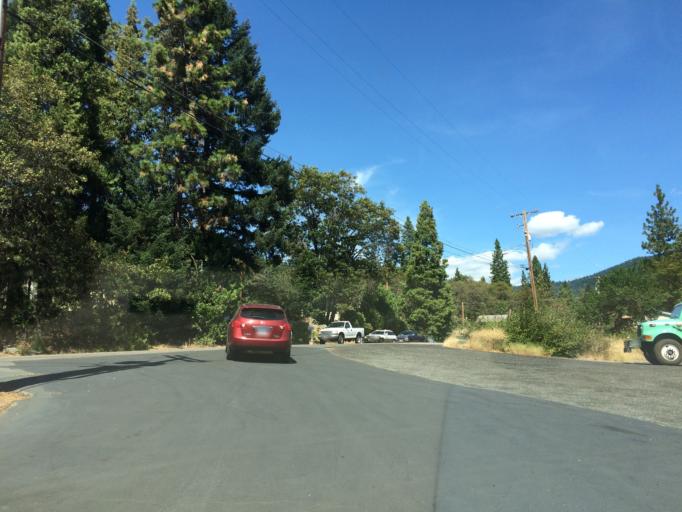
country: US
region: California
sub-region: Siskiyou County
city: Dunsmuir
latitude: 41.1954
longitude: -122.2819
